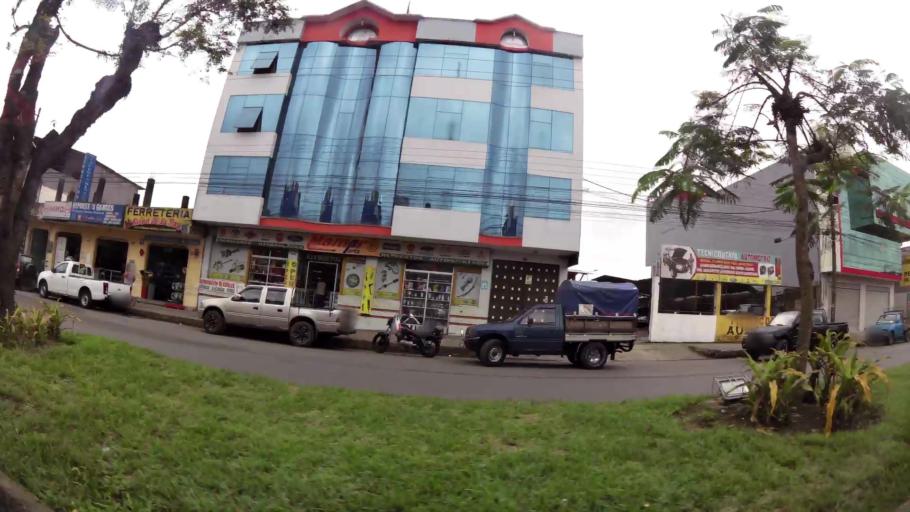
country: EC
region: Santo Domingo de los Tsachilas
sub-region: Canton Santo Domingo de los Colorados
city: Santo Domingo de los Colorados
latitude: -0.2415
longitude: -79.1705
